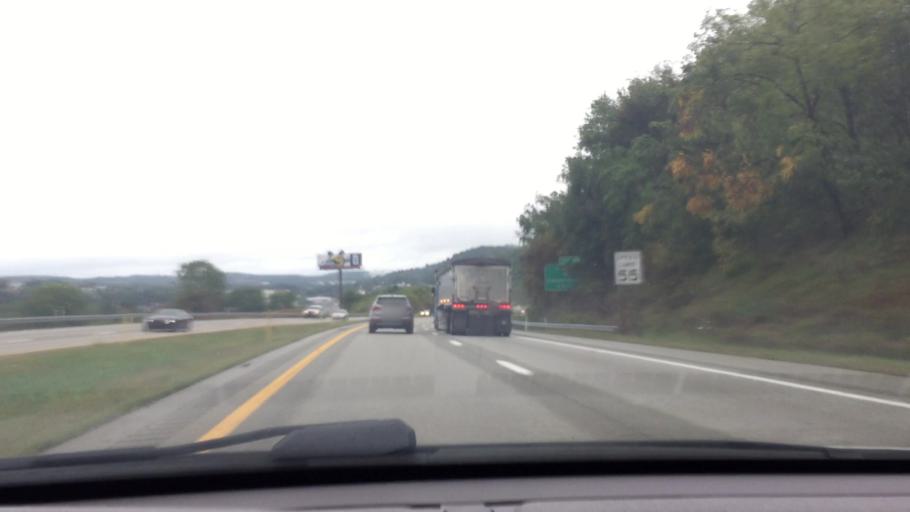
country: US
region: Pennsylvania
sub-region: Washington County
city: Canonsburg
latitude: 40.2513
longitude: -80.1911
